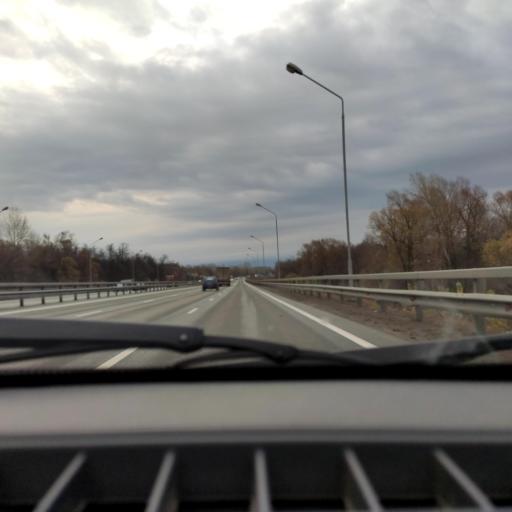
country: RU
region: Bashkortostan
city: Ufa
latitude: 54.6603
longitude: 55.8775
